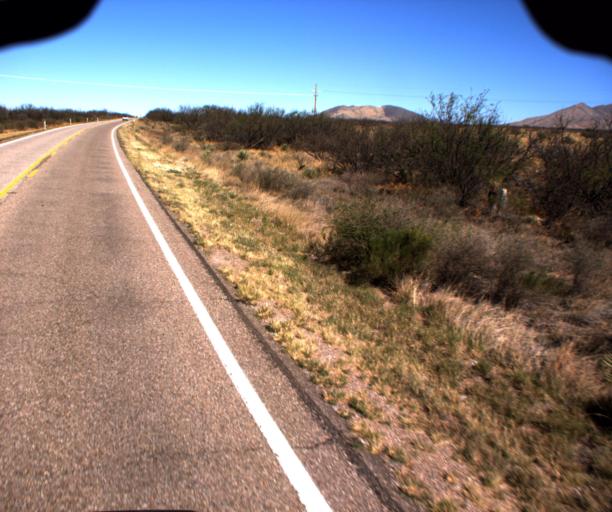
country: US
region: Arizona
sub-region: Cochise County
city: Huachuca City
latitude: 31.6961
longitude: -110.4207
